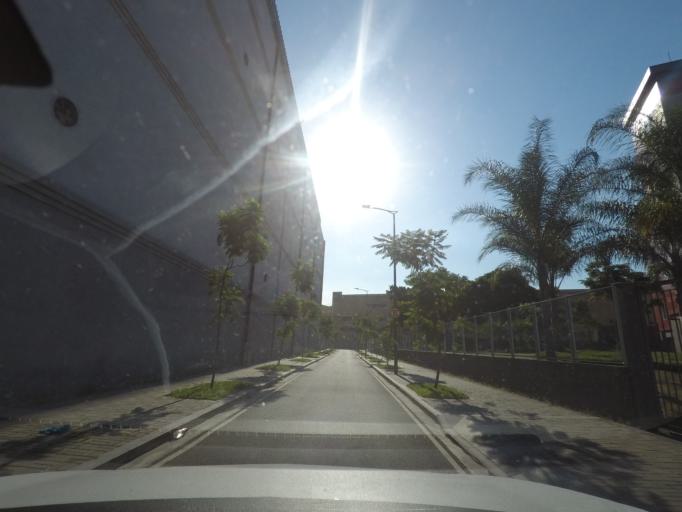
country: BR
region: Rio de Janeiro
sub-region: Rio De Janeiro
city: Rio de Janeiro
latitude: -22.8959
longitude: -43.1955
